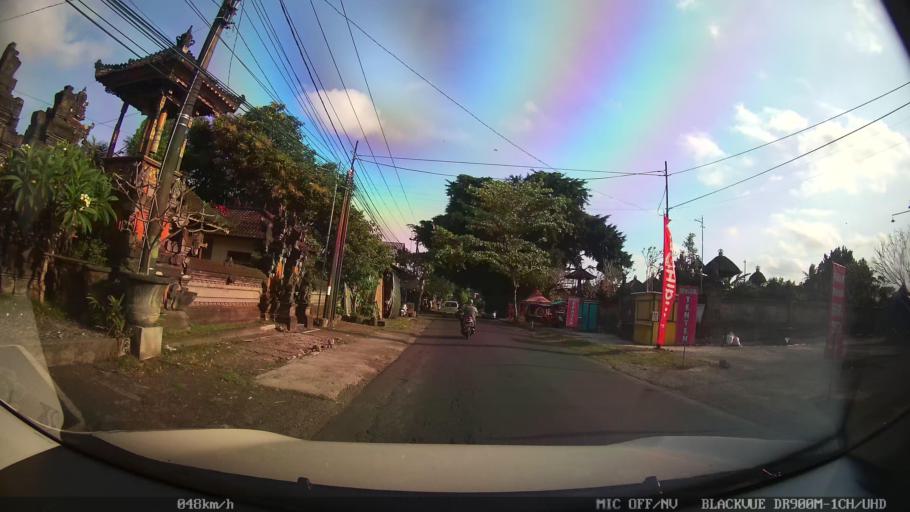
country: ID
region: Bali
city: Banjar Parekan
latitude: -8.5754
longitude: 115.2181
